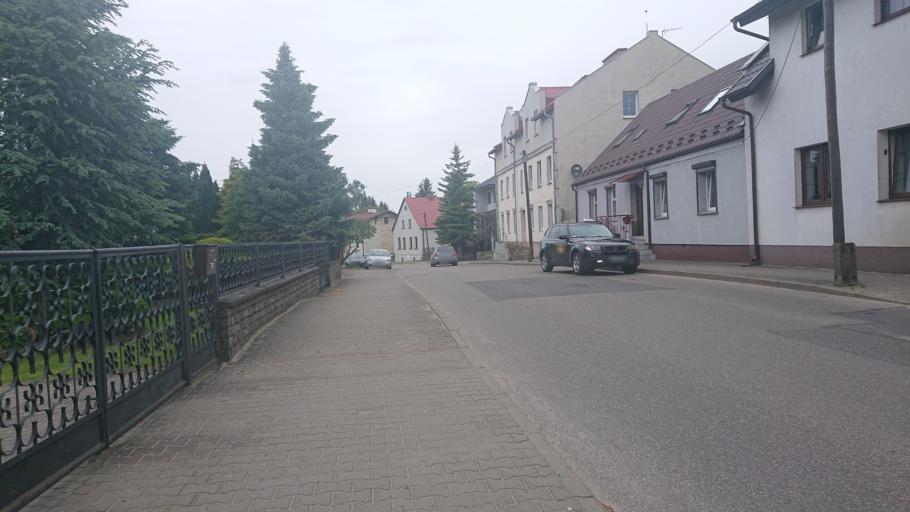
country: PL
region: Pomeranian Voivodeship
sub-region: Powiat chojnicki
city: Chojnice
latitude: 53.6961
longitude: 17.5667
